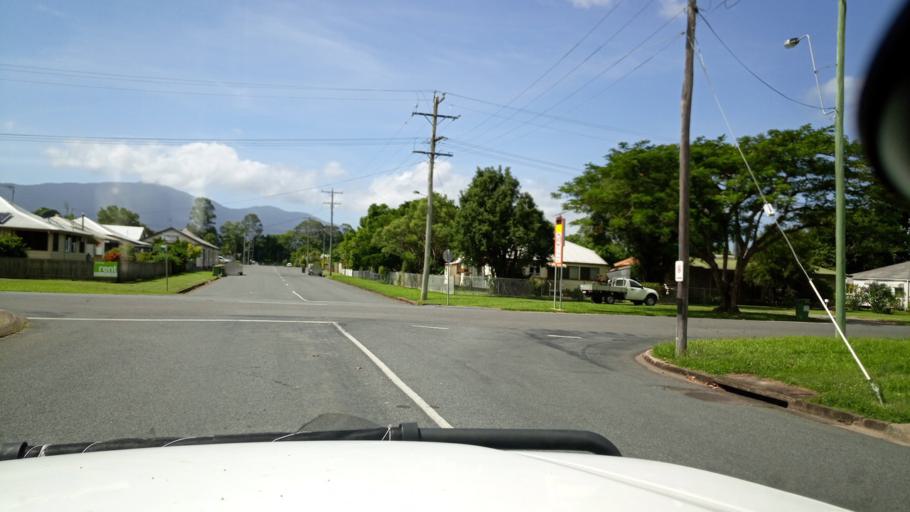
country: AU
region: Queensland
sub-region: Cairns
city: Woree
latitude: -17.0893
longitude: 145.7851
